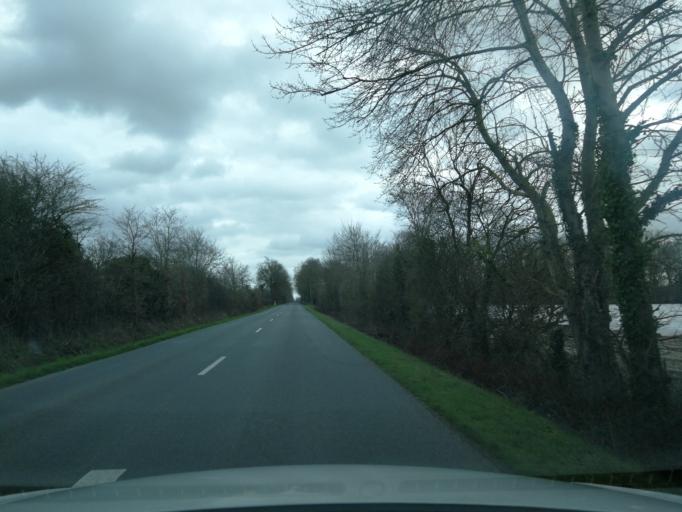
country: FR
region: Pays de la Loire
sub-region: Departement de la Loire-Atlantique
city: Geneston
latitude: 47.0344
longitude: -1.5039
